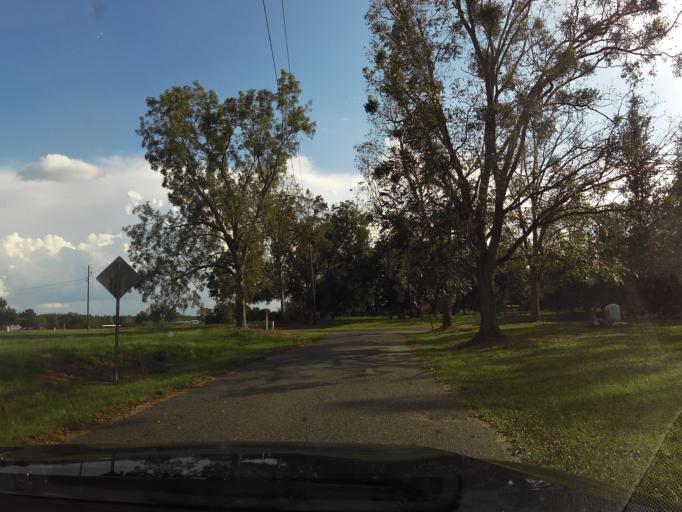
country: US
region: Georgia
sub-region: Brooks County
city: Quitman
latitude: 30.7873
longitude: -83.6354
